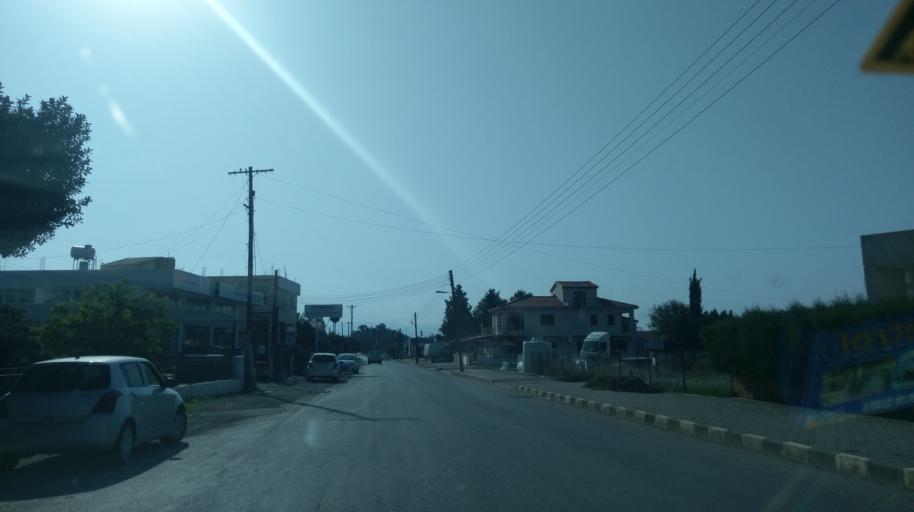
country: CY
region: Lefkosia
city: Morfou
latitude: 35.1958
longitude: 32.9846
